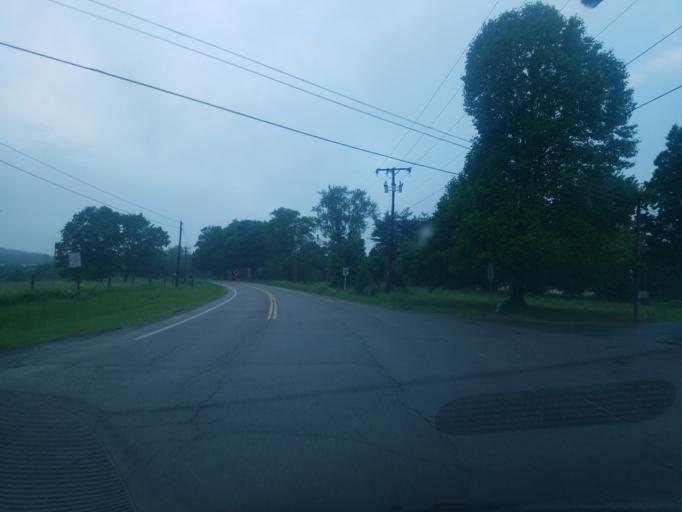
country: US
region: Ohio
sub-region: Columbiana County
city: Salem
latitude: 40.8282
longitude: -80.9148
